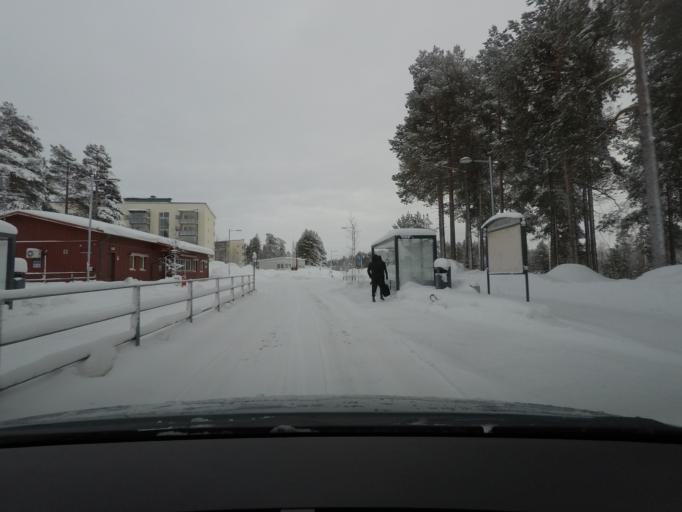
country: SE
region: Norrbotten
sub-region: Lulea Kommun
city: Lulea
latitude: 65.5922
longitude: 22.1891
